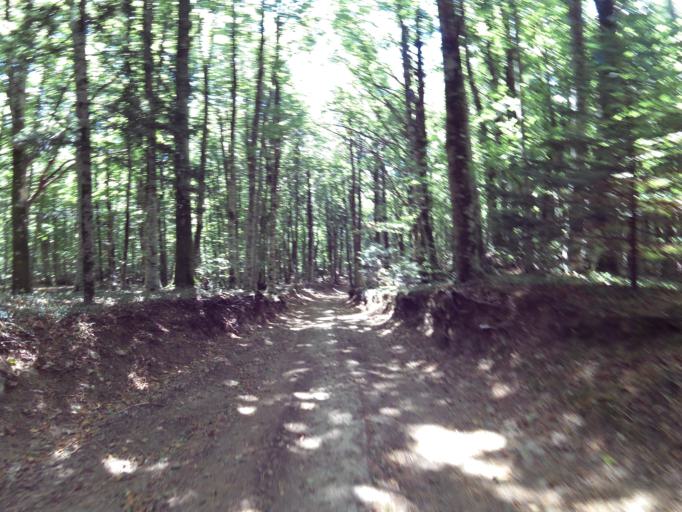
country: IT
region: Calabria
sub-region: Provincia di Vibo-Valentia
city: Mongiana
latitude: 38.5207
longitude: 16.3447
